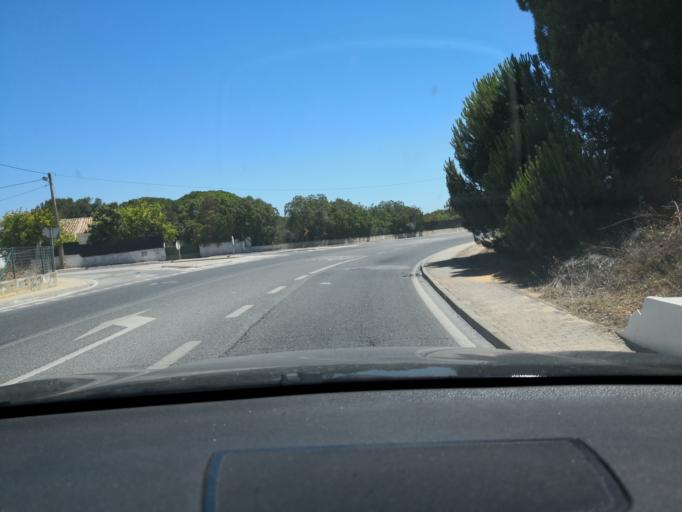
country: PT
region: Faro
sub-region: Albufeira
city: Ferreiras
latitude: 37.1088
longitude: -8.2036
